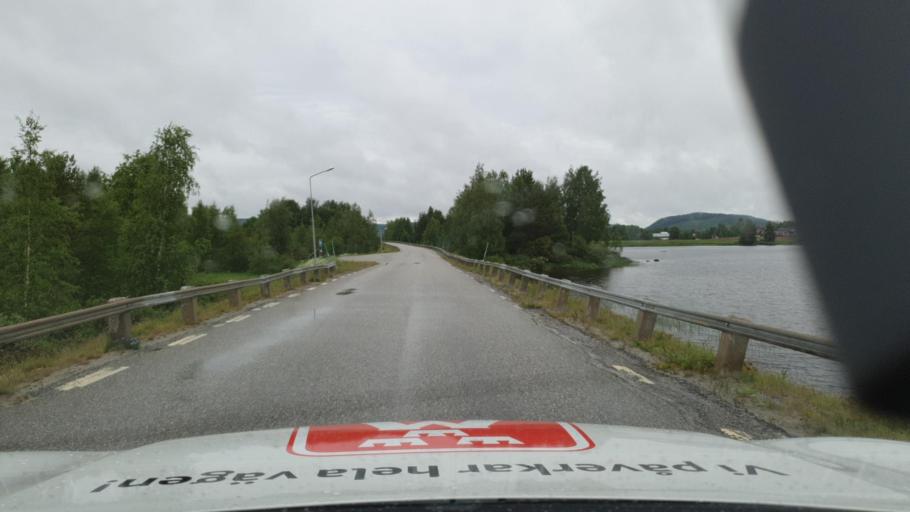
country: SE
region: Vaesterbotten
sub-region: Asele Kommun
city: Asele
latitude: 64.0056
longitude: 17.2682
